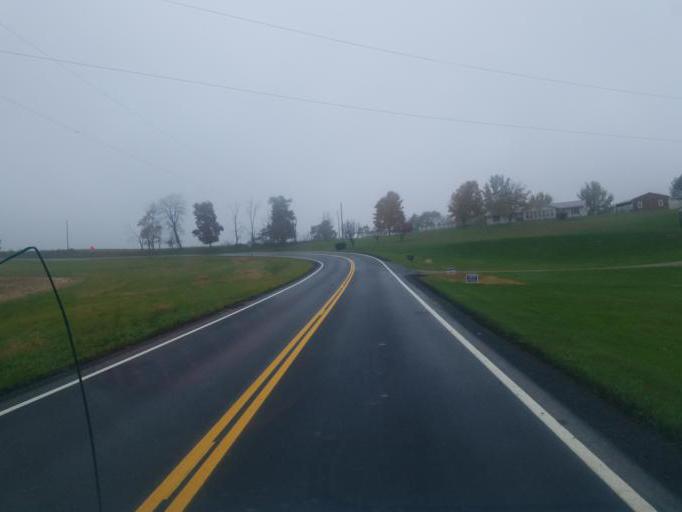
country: US
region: Ohio
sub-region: Morgan County
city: McConnelsville
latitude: 39.5674
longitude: -81.8370
